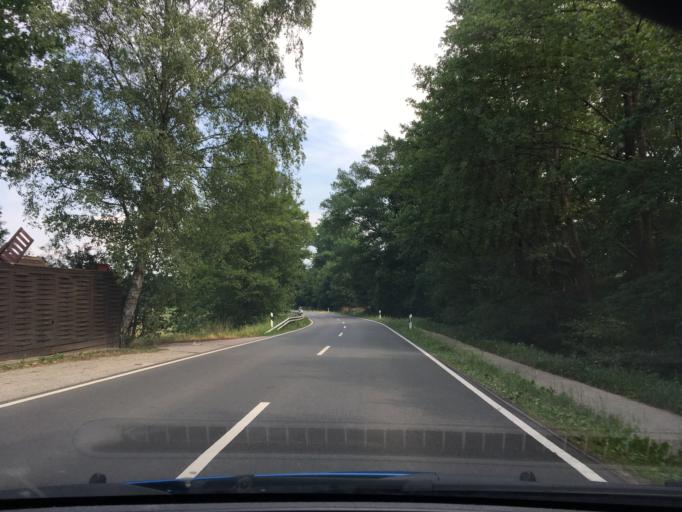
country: DE
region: Lower Saxony
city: Asendorf
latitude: 53.2670
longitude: 9.9737
